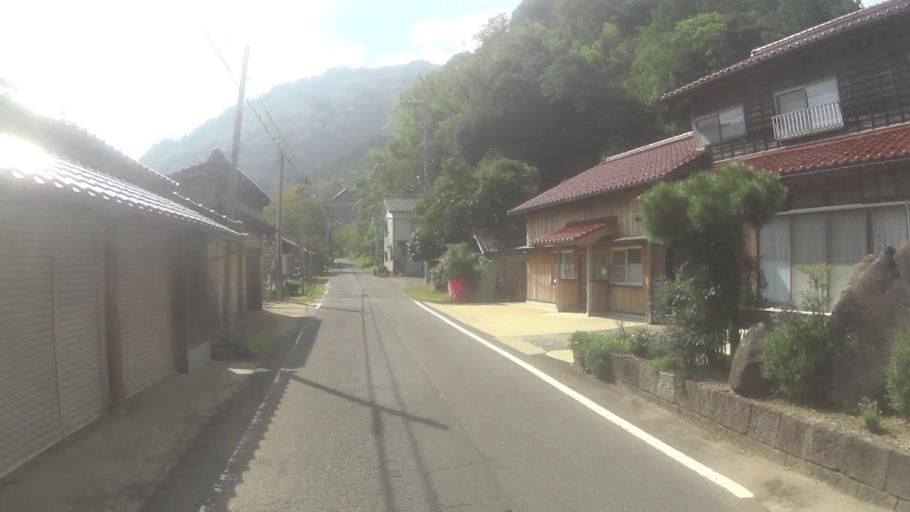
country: JP
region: Kyoto
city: Miyazu
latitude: 35.7378
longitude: 135.1549
